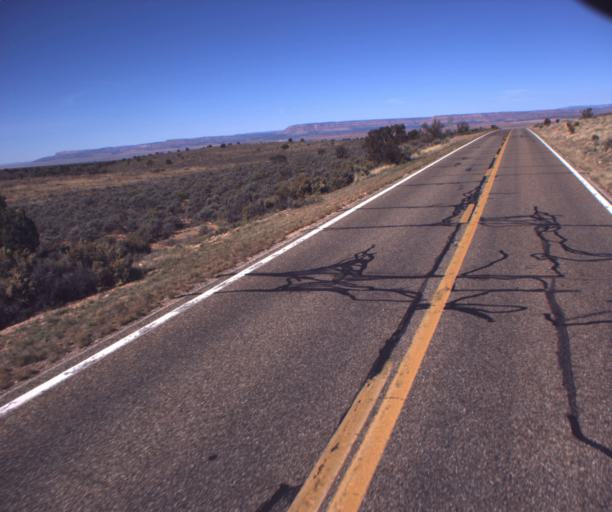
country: US
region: Arizona
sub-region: Coconino County
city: Fredonia
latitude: 36.8784
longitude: -112.3360
